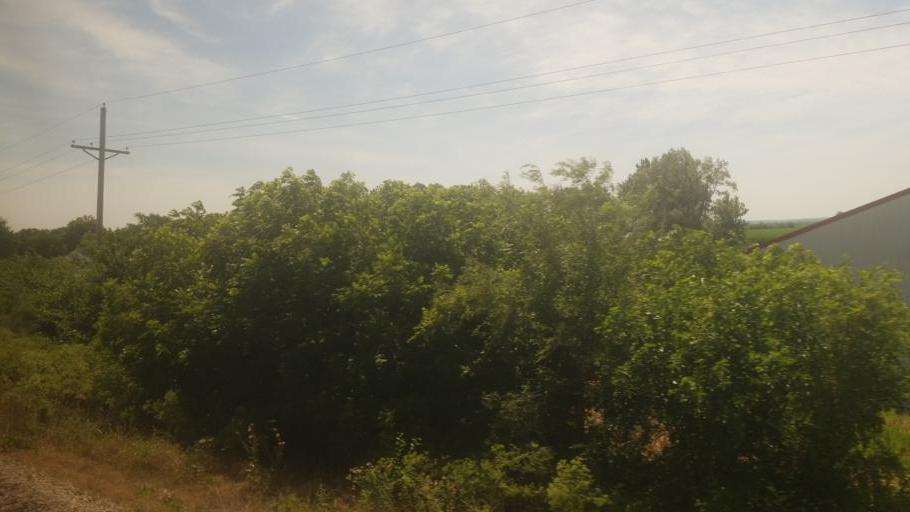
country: US
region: Missouri
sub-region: Carroll County
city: Carrollton
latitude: 39.3015
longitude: -93.6866
